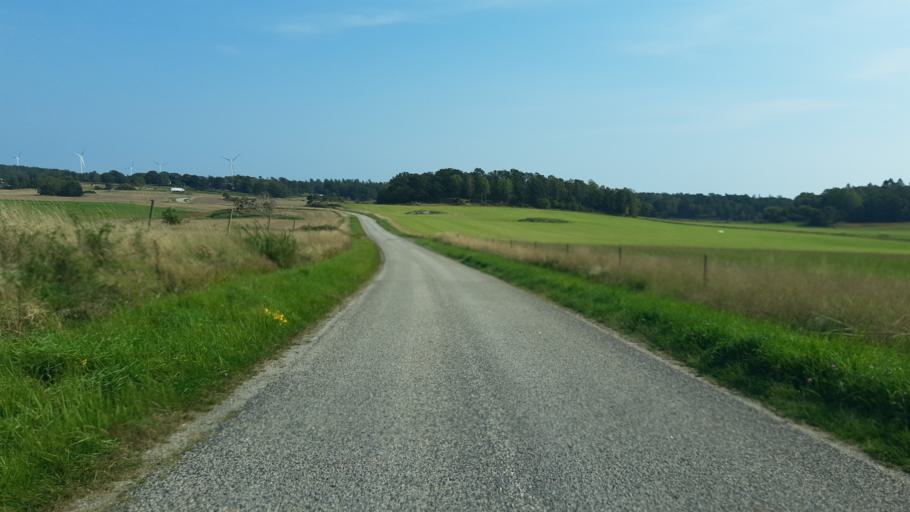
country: SE
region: Blekinge
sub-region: Ronneby Kommun
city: Brakne-Hoby
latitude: 56.1968
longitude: 15.1062
